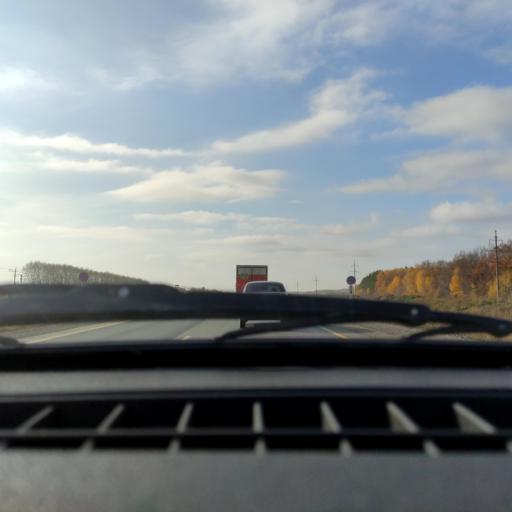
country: RU
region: Bashkortostan
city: Kabakovo
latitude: 54.7172
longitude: 56.2347
